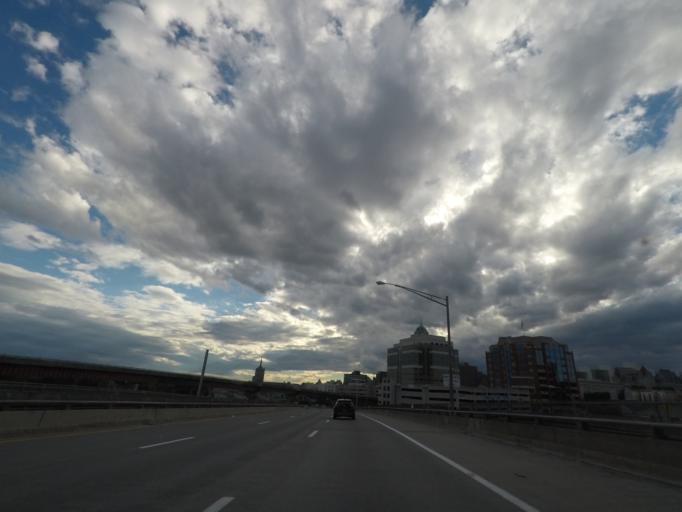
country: US
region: New York
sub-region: Albany County
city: Albany
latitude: 42.6545
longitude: -73.7456
